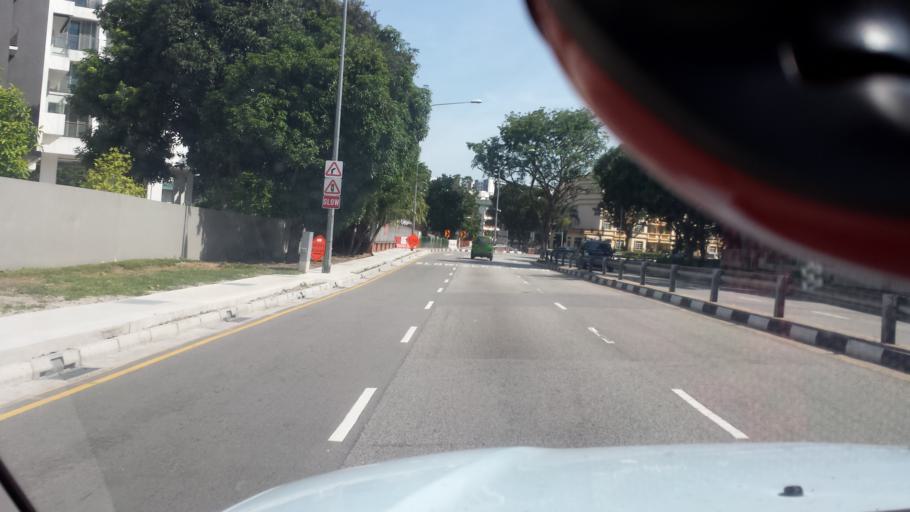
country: SG
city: Singapore
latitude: 1.3133
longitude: 103.8918
